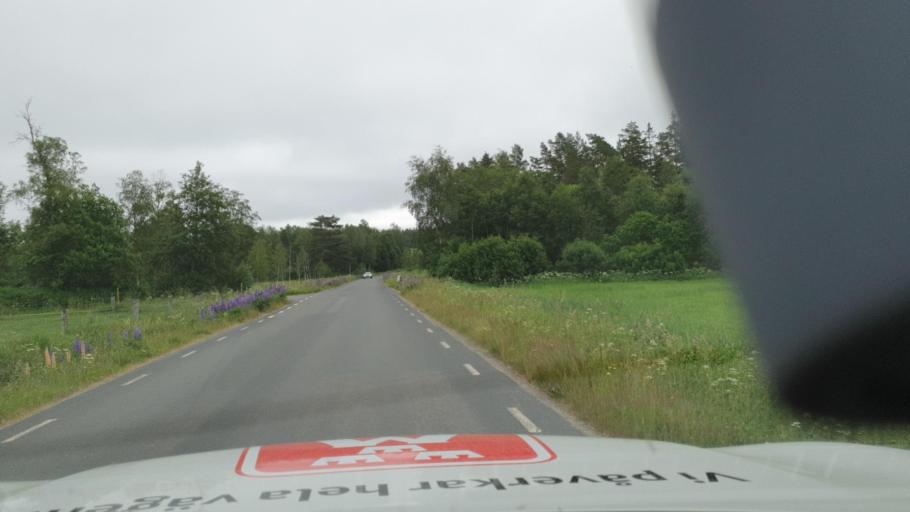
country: SE
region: Joenkoeping
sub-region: Mullsjo Kommun
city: Mullsjoe
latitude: 57.8854
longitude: 13.8136
